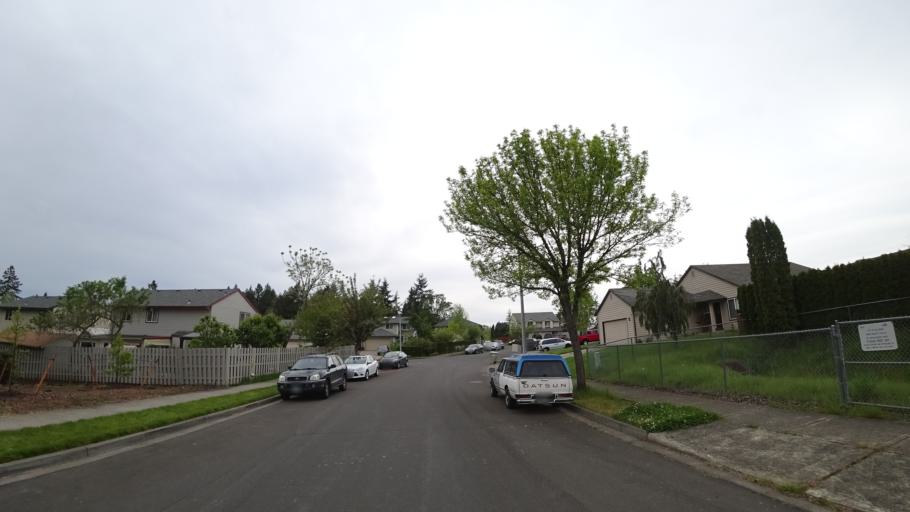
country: US
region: Oregon
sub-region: Washington County
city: Aloha
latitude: 45.5105
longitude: -122.9185
